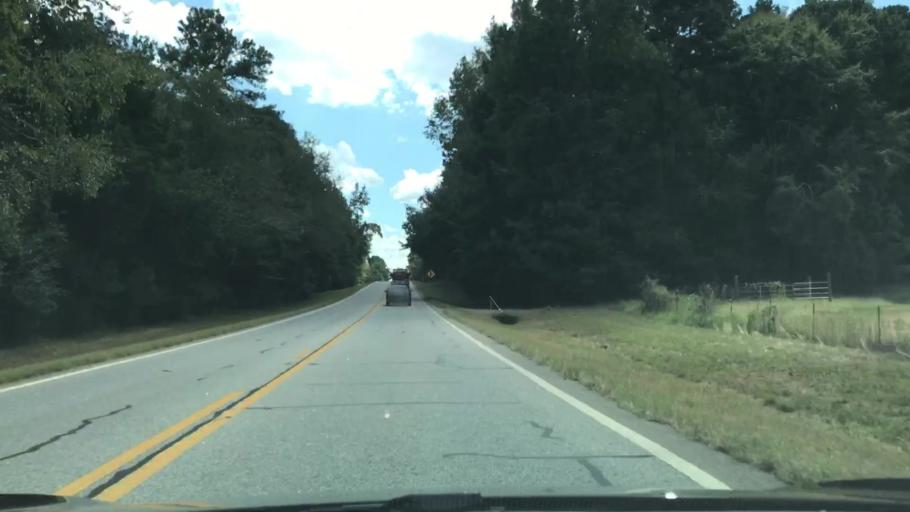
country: US
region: Georgia
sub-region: Oconee County
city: Watkinsville
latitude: 33.7730
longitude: -83.3105
